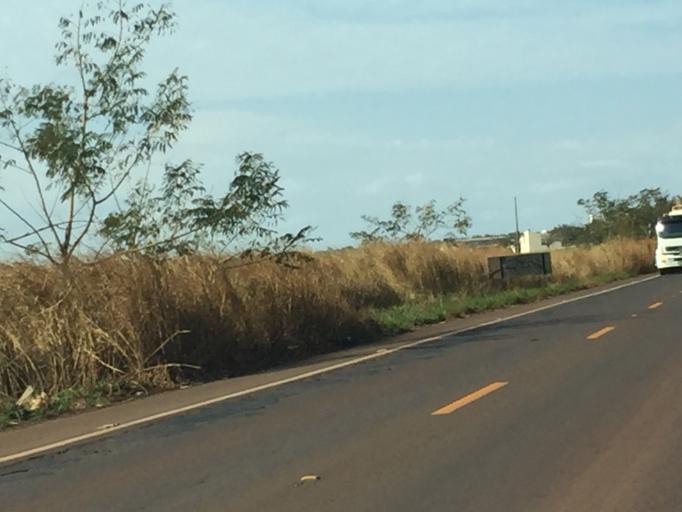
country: BR
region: Sao Paulo
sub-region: Sertaozinho
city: Sertaozinho
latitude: -21.2529
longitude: -47.9797
